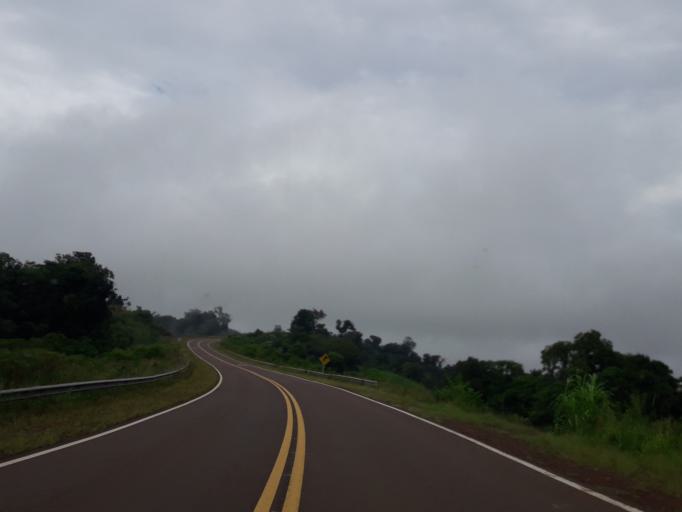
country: AR
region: Misiones
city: Bernardo de Irigoyen
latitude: -26.4038
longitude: -53.8212
